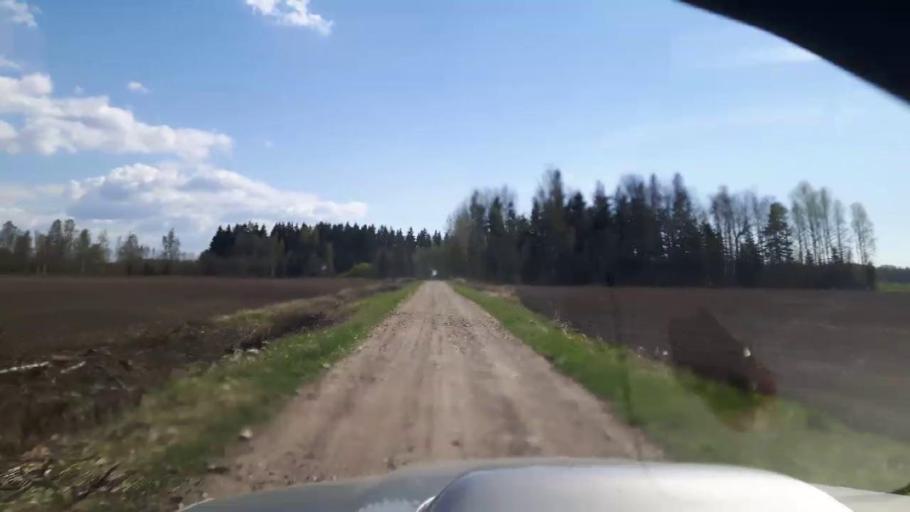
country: EE
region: Paernumaa
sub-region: Tootsi vald
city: Tootsi
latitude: 58.4506
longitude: 24.8452
